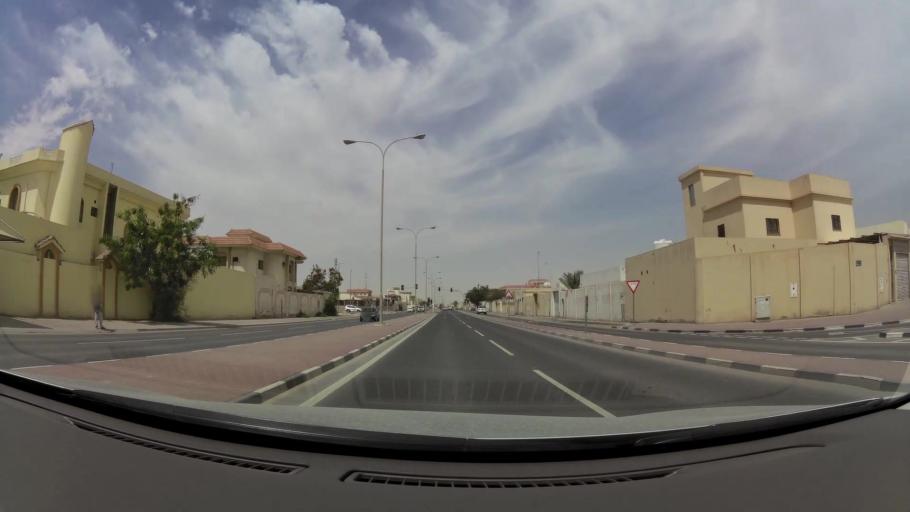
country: QA
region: Baladiyat ar Rayyan
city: Ar Rayyan
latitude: 25.2887
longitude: 51.4166
